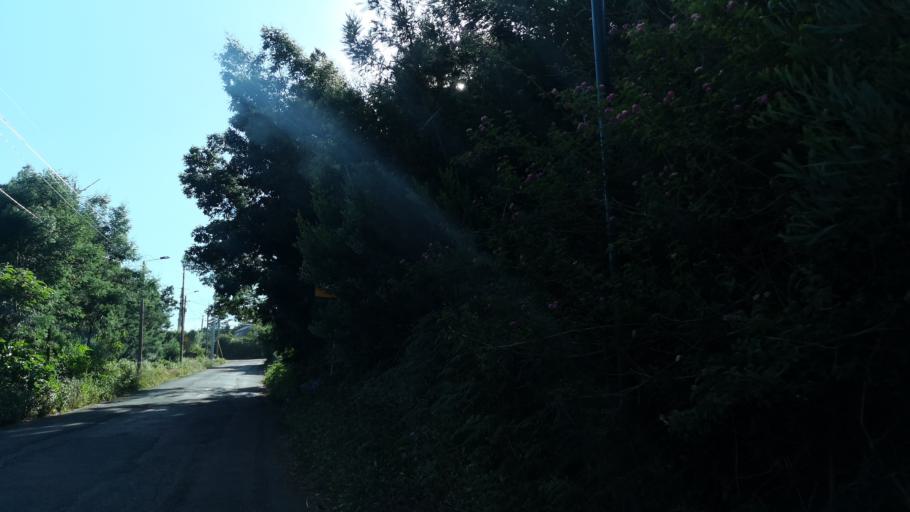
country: PT
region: Madeira
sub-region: Santa Cruz
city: Camacha
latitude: 32.6673
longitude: -16.8397
